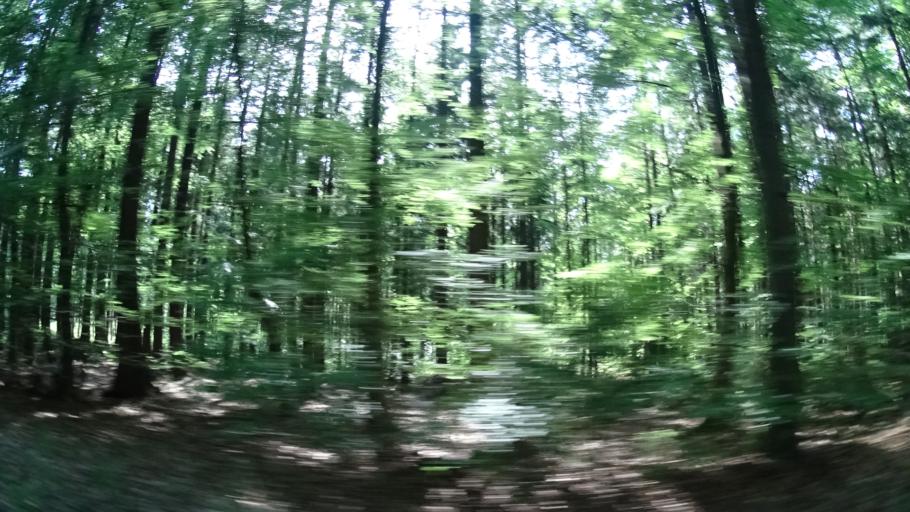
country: DE
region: Hesse
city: Michelstadt
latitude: 49.6955
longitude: 9.0863
